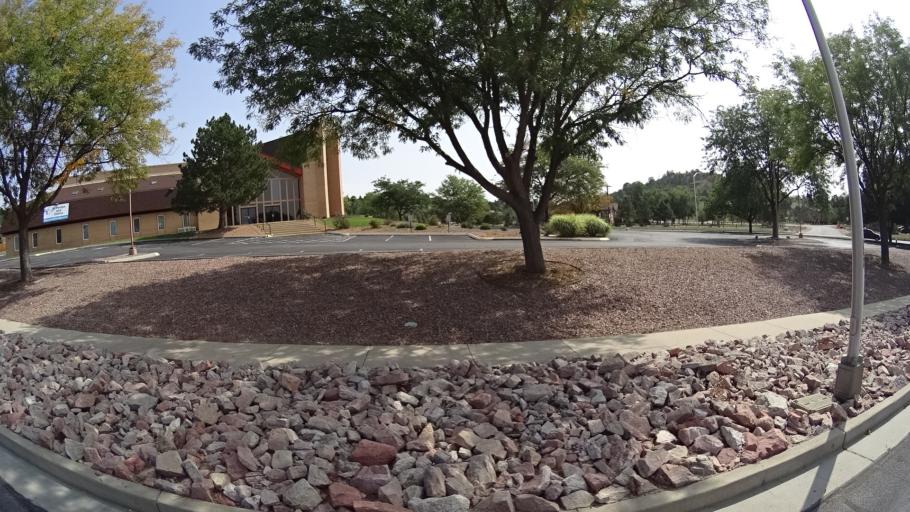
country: US
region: Colorado
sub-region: El Paso County
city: Cimarron Hills
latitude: 38.8625
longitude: -104.7478
